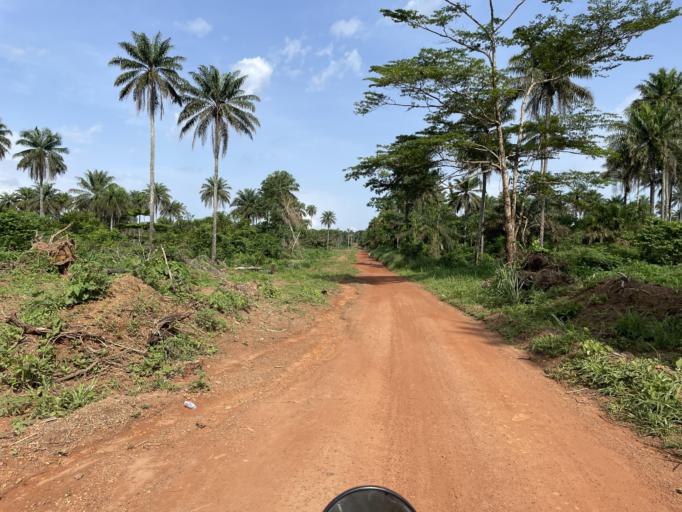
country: SL
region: Southern Province
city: Pujehun
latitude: 7.3715
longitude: -11.7428
